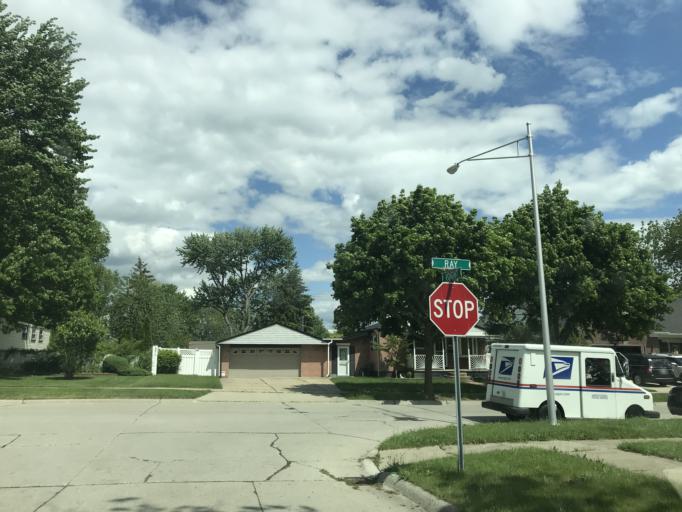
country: US
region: Michigan
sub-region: Wayne County
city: Riverview
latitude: 42.1758
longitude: -83.1879
